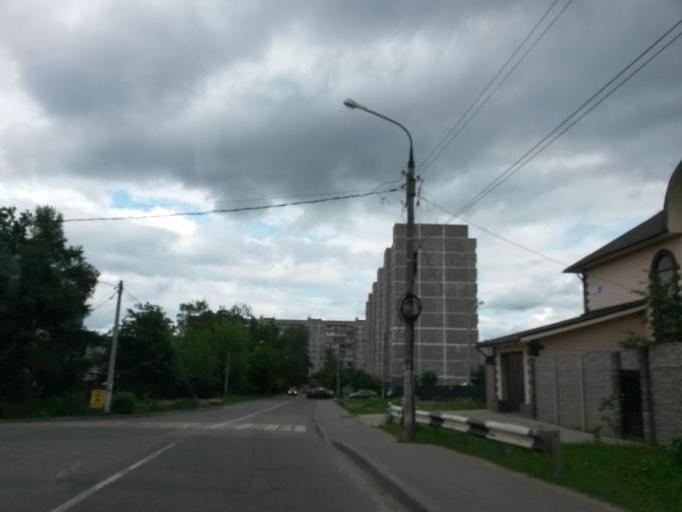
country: RU
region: Moskovskaya
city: Klimovsk
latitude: 55.3594
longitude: 37.5358
